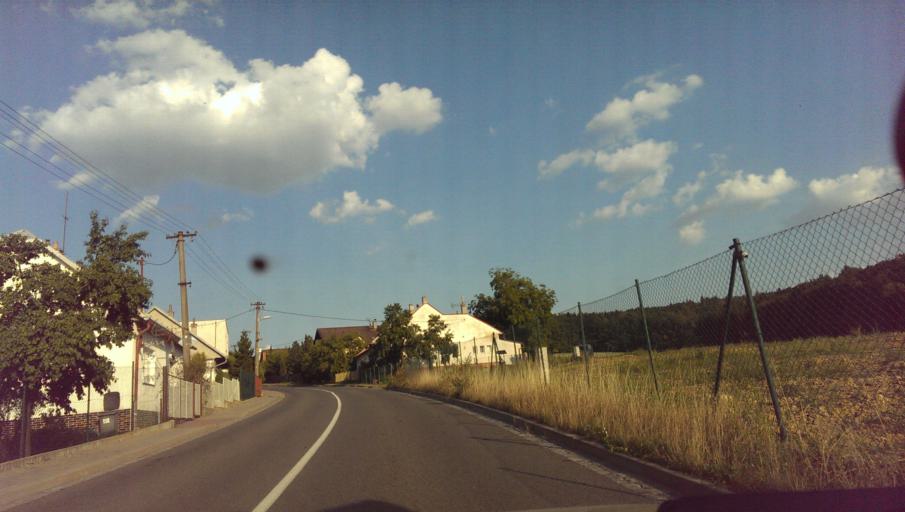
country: CZ
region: Zlin
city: Lukov
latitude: 49.2646
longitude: 17.7300
